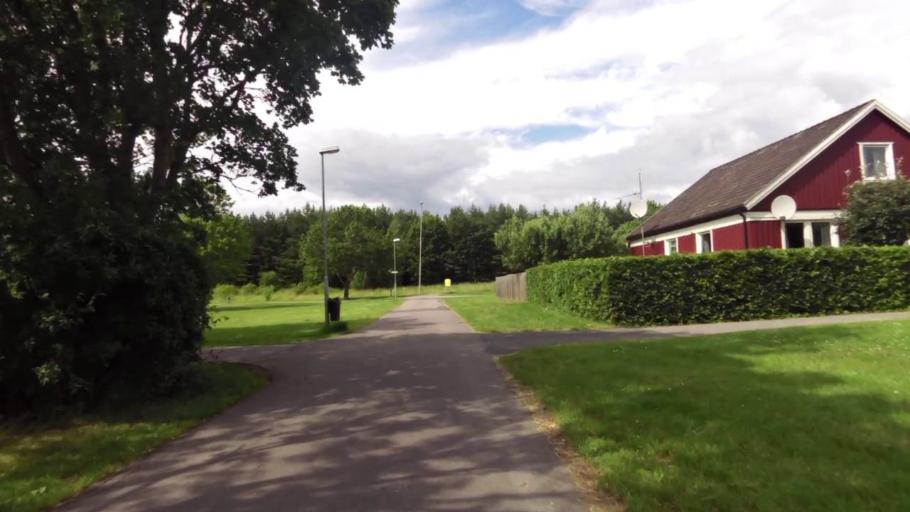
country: SE
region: OEstergoetland
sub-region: Linkopings Kommun
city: Malmslatt
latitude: 58.4185
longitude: 15.5610
